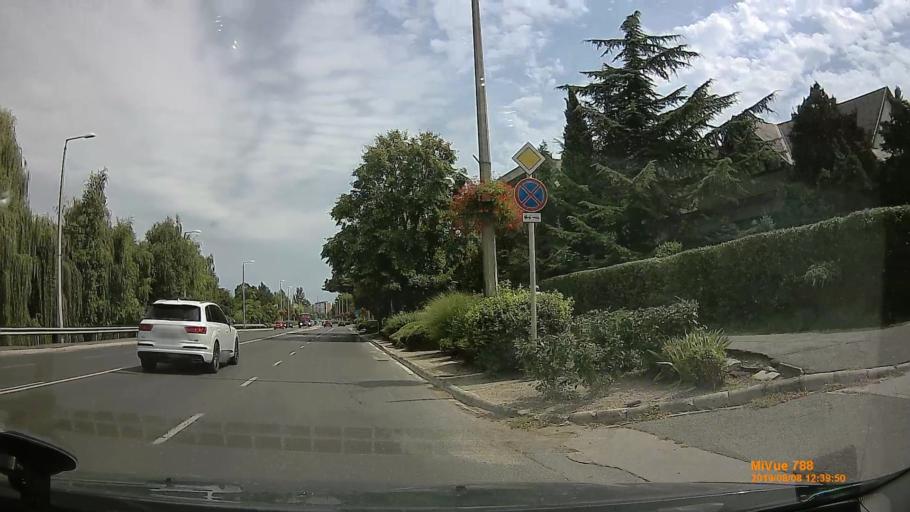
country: HU
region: Somogy
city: Siofok
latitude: 46.9008
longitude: 18.0357
